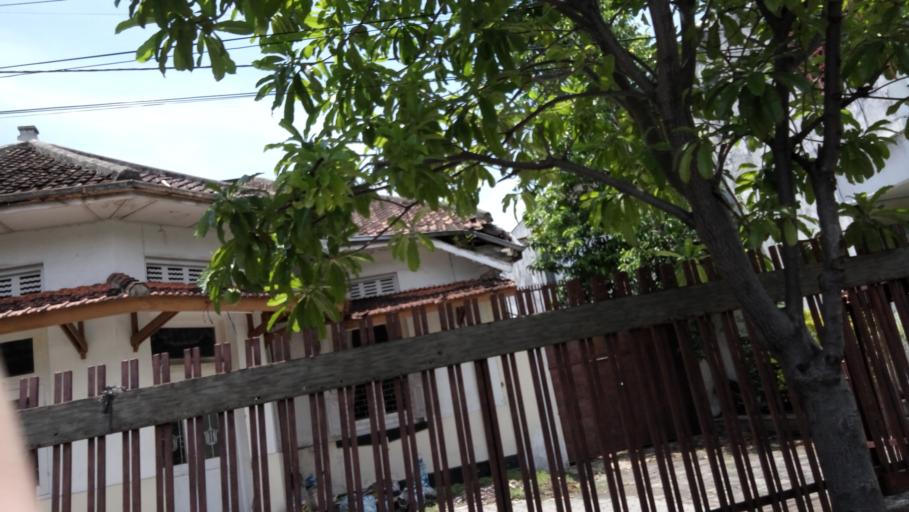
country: ID
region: East Java
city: Malang
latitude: -7.9866
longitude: 112.6285
